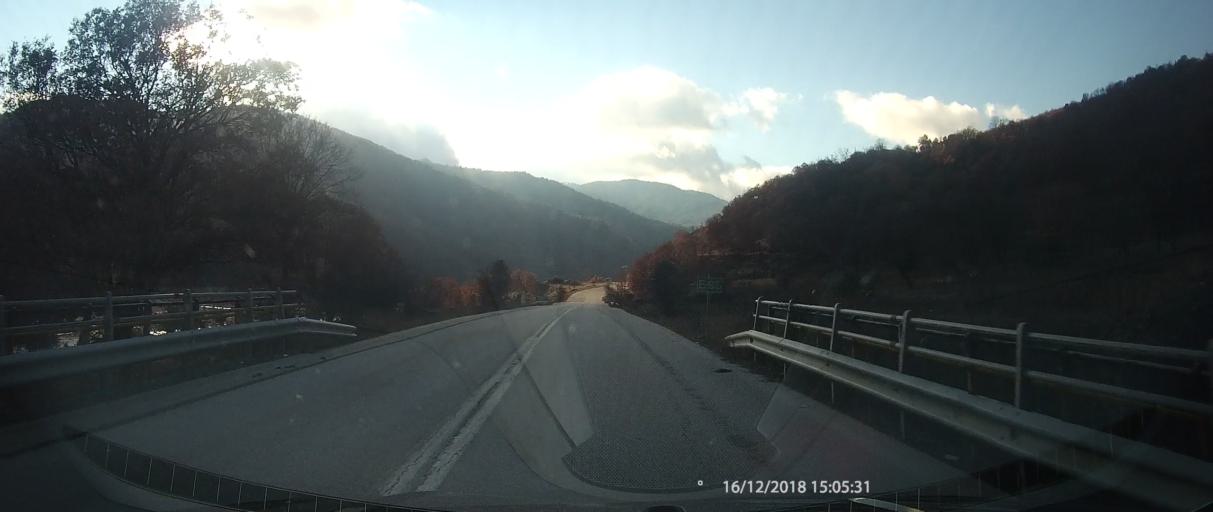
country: GR
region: West Macedonia
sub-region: Nomos Kastorias
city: Nestorio
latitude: 40.2226
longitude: 20.9578
